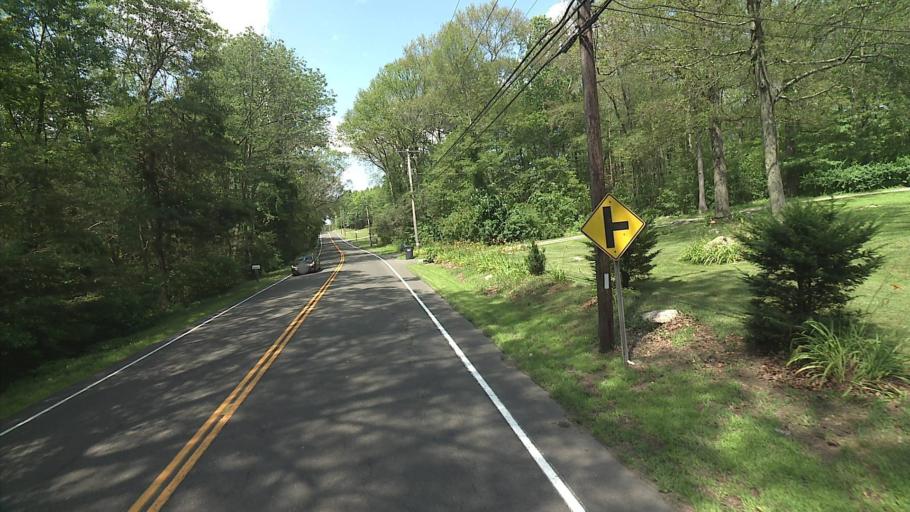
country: US
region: Connecticut
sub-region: Middlesex County
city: Higganum
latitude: 41.4410
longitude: -72.5561
